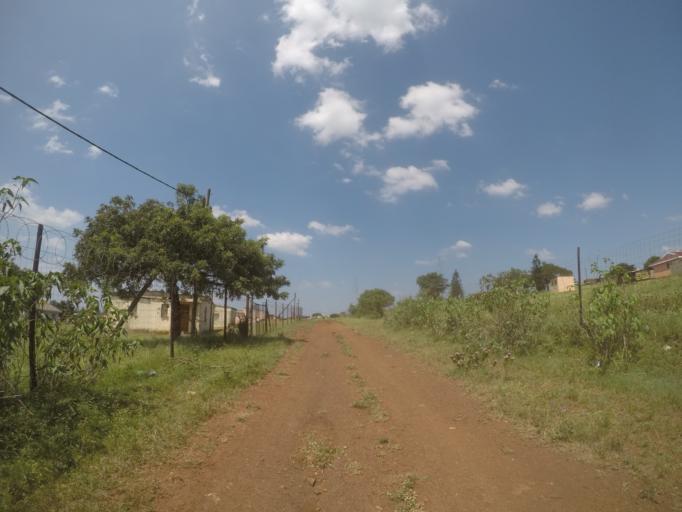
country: ZA
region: KwaZulu-Natal
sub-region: uThungulu District Municipality
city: Empangeni
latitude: -28.5930
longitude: 31.7383
